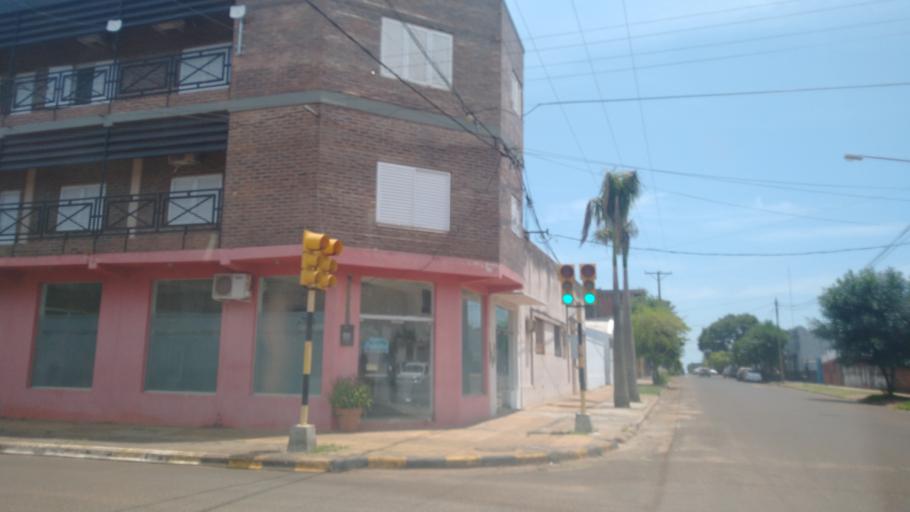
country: AR
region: Corrientes
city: Santo Tome
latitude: -28.5509
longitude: -56.0379
